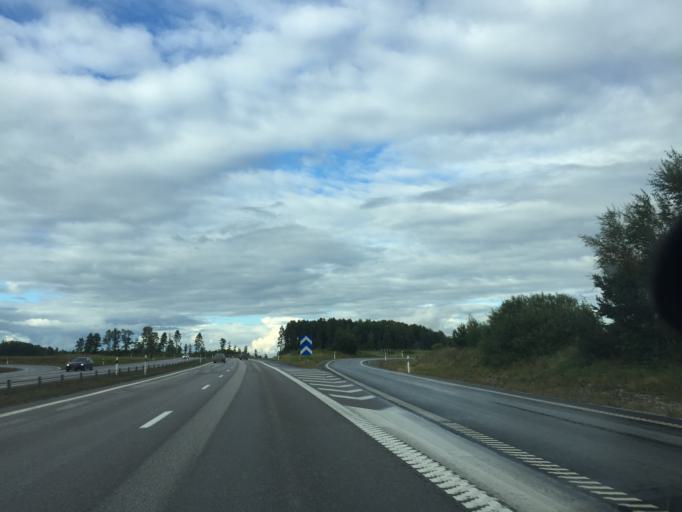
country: SE
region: Vaestmanland
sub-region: Arboga Kommun
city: Arboga
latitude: 59.4128
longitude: 15.7693
